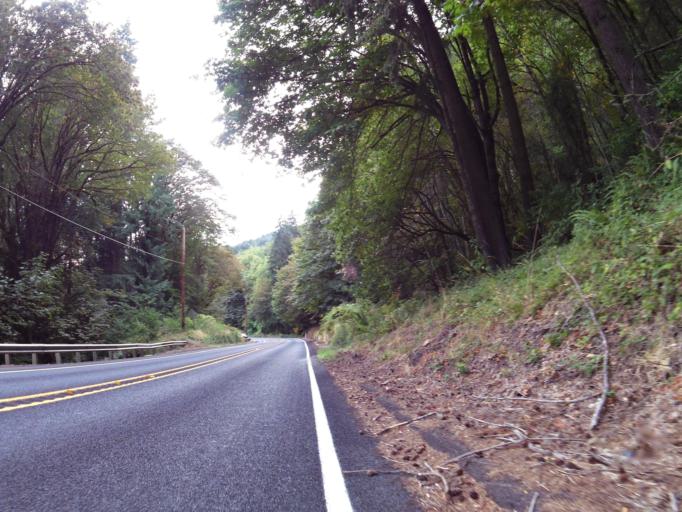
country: US
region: Oregon
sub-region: Columbia County
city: Clatskanie
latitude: 46.1737
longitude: -123.2253
